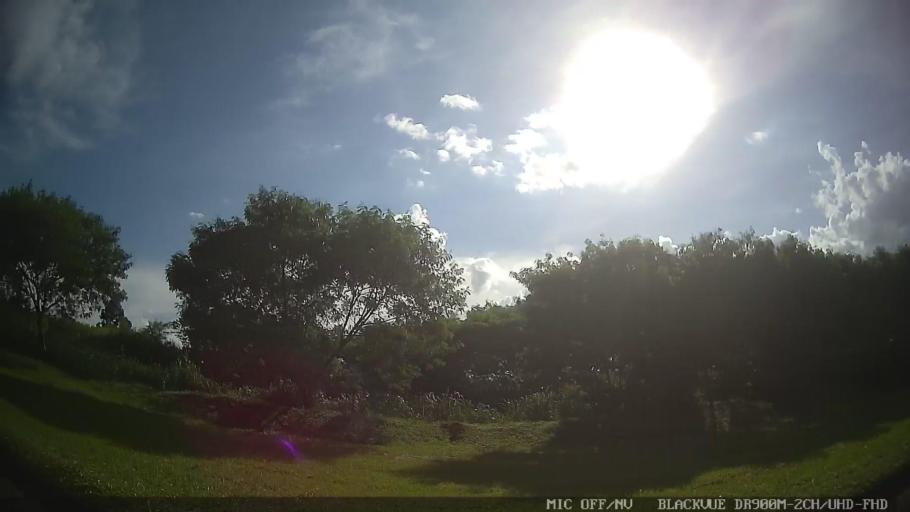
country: BR
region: Sao Paulo
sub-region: Laranjal Paulista
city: Laranjal Paulista
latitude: -23.0751
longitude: -47.8100
